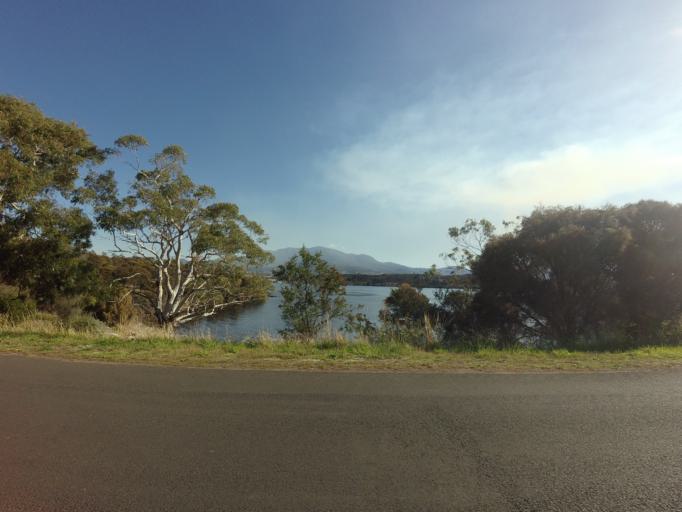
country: AU
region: Tasmania
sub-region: Clarence
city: Bellerive
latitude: -42.8691
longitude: 147.3540
